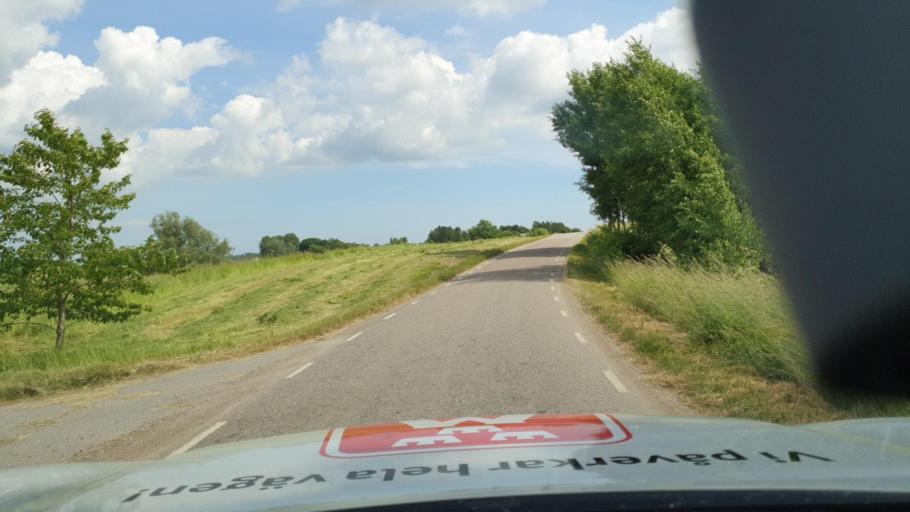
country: SE
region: Skane
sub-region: Skurups Kommun
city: Skurup
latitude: 55.5220
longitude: 13.4720
